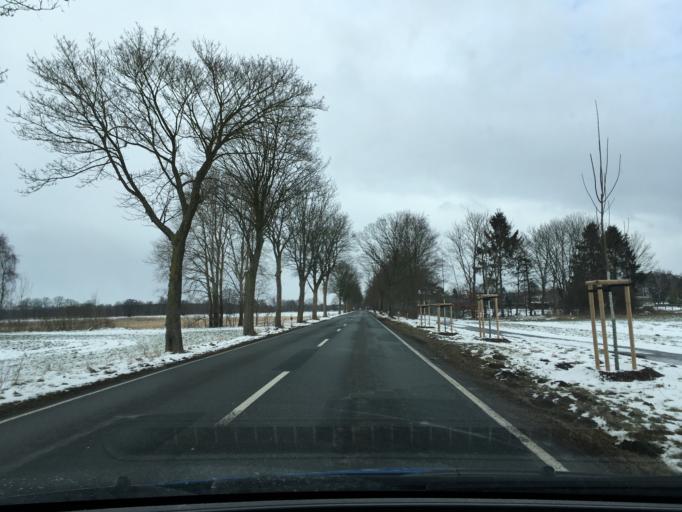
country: DE
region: Lower Saxony
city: Wulfsen
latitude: 53.3163
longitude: 10.1740
